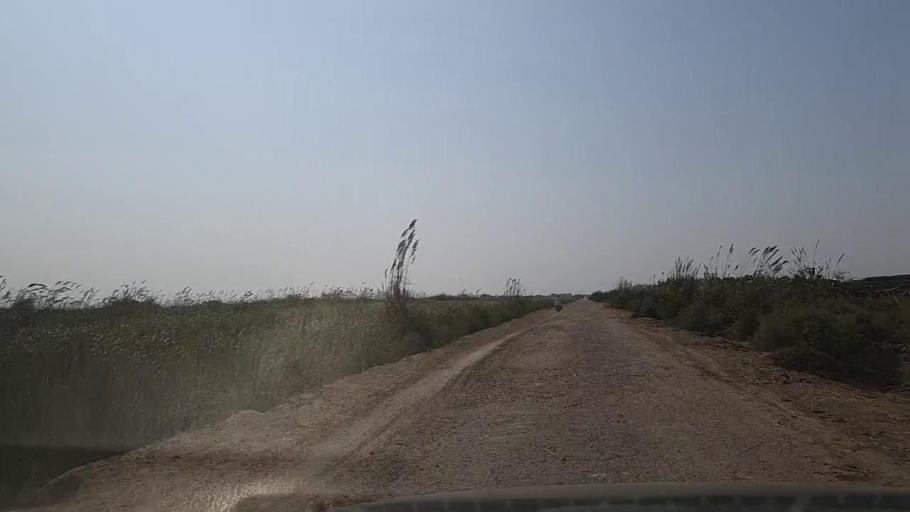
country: PK
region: Sindh
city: Mirpur Sakro
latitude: 24.3719
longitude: 67.6515
